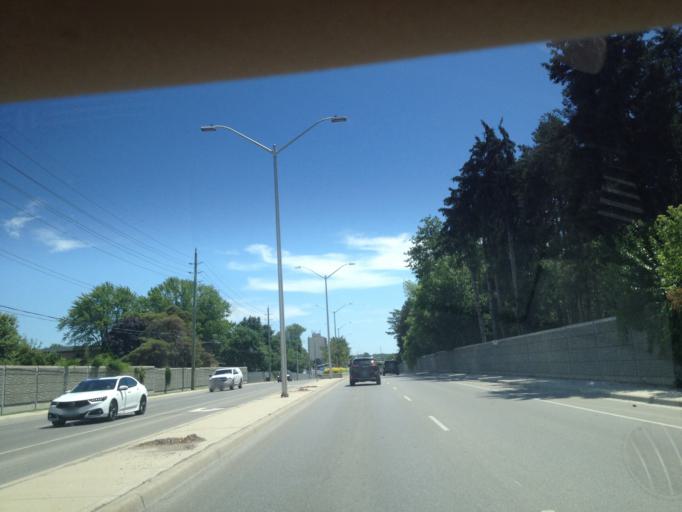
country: CA
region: Ontario
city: London
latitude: 42.9808
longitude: -81.3231
